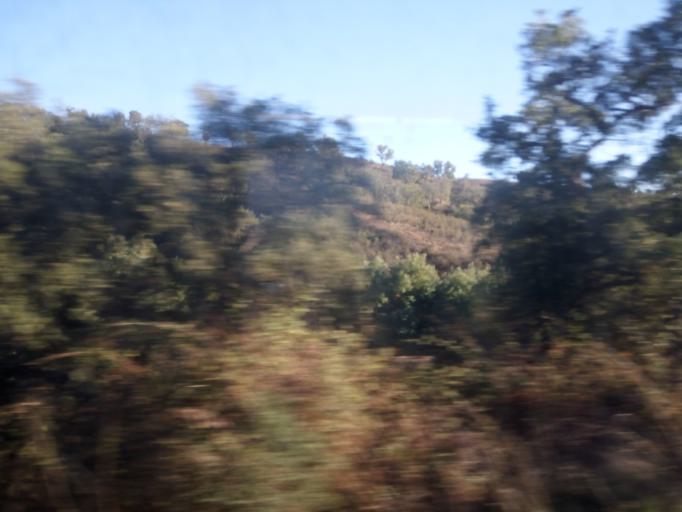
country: PT
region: Beja
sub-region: Odemira
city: Odemira
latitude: 37.5857
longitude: -8.4922
